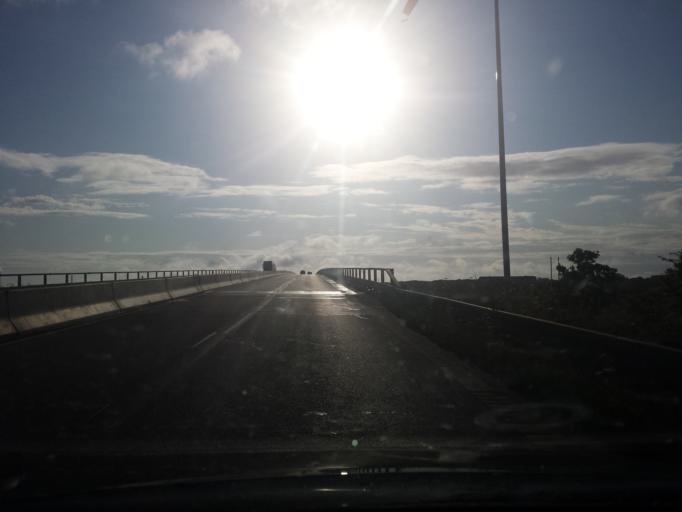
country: DK
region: South Denmark
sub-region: Sonderborg Kommune
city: Dybbol
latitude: 54.9215
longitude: 9.7608
